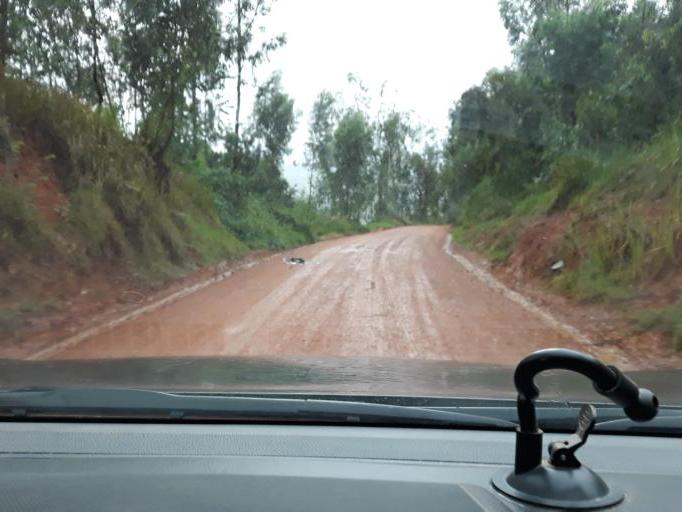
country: CD
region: Eastern Province
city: Bunia
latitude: 1.7838
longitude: 30.3889
